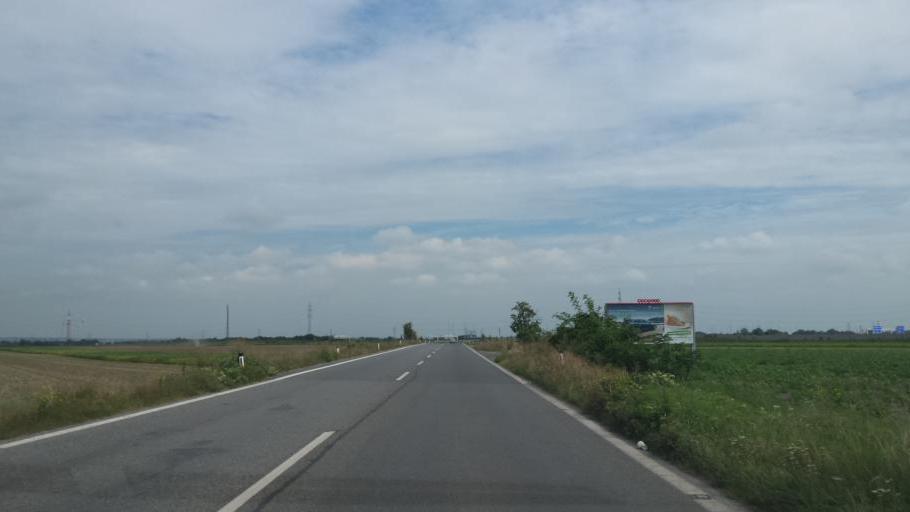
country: AT
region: Lower Austria
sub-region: Politischer Bezirk Ganserndorf
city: Aderklaa
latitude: 48.2796
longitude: 16.5057
